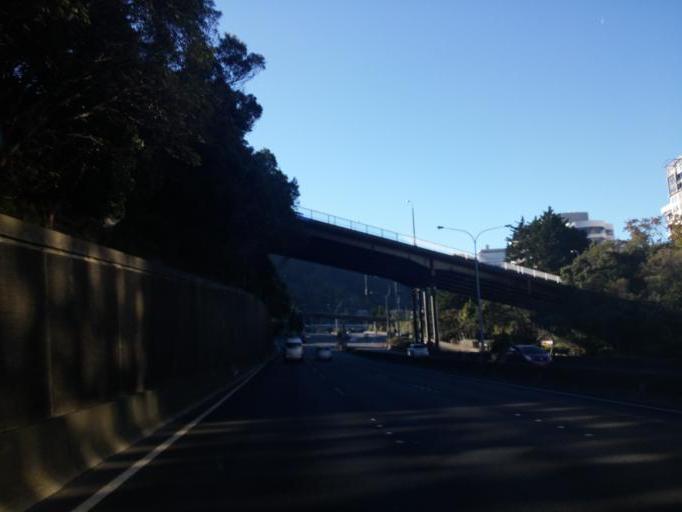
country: NZ
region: Wellington
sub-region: Wellington City
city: Wellington
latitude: -41.2808
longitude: 174.7735
